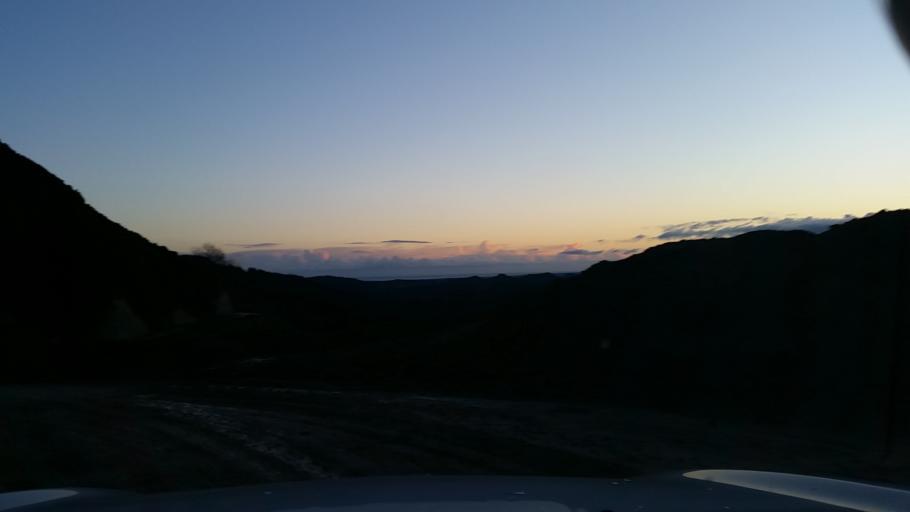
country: NZ
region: Manawatu-Wanganui
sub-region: Wanganui District
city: Wanganui
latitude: -39.7575
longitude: 174.8858
